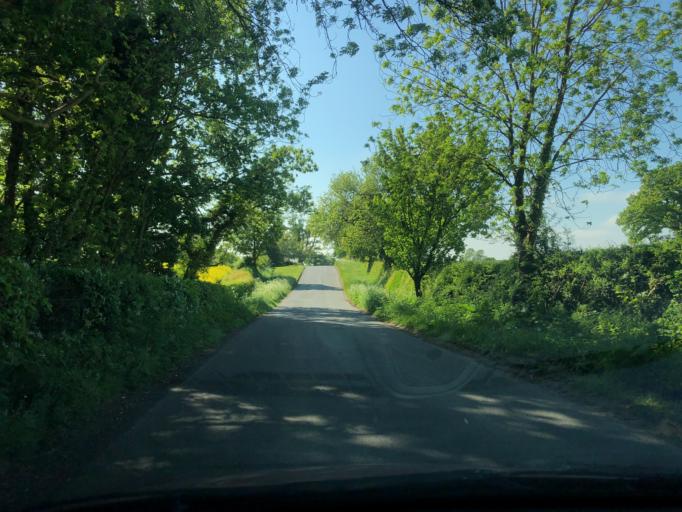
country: GB
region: England
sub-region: North Yorkshire
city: Northallerton
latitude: 54.3256
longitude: -1.3982
